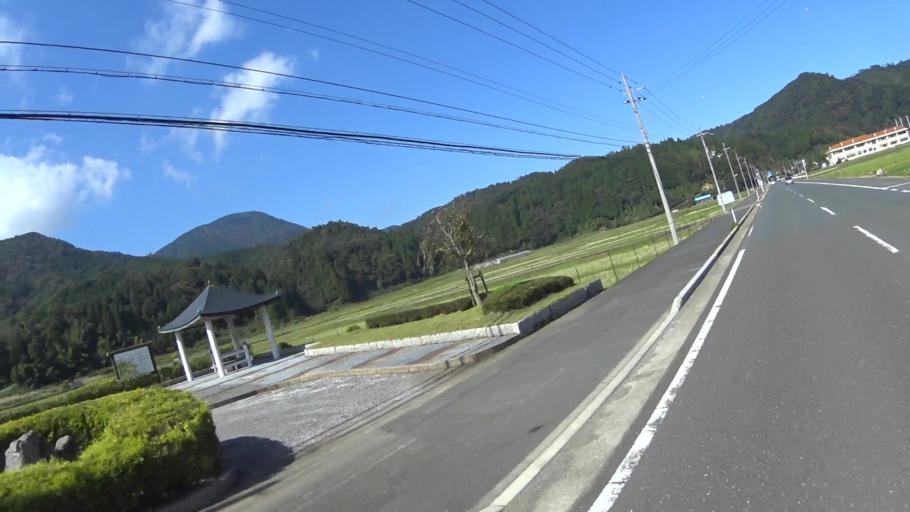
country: JP
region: Kyoto
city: Miyazu
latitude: 35.7247
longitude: 135.2549
